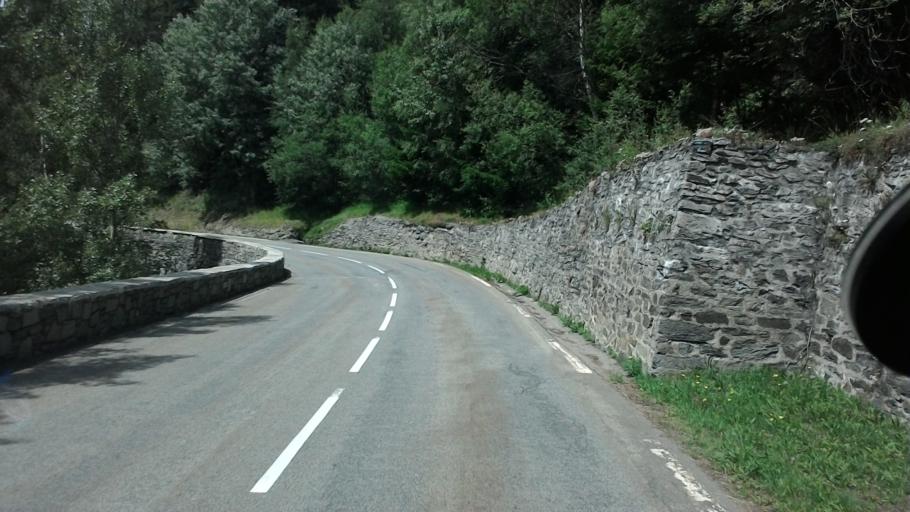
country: FR
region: Rhone-Alpes
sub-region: Departement de la Savoie
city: Seez
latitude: 45.6254
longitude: 6.8351
